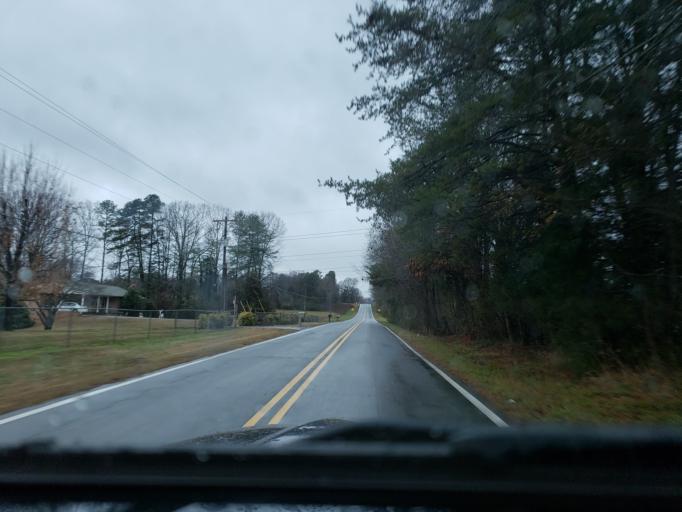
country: US
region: North Carolina
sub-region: Cleveland County
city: White Plains
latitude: 35.1848
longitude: -81.3775
